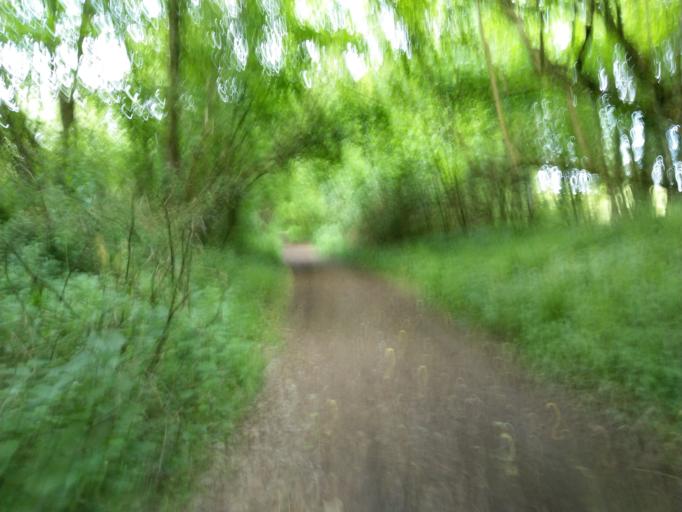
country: FR
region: Picardie
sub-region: Departement de l'Aisne
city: Guise
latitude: 49.9245
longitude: 3.5898
